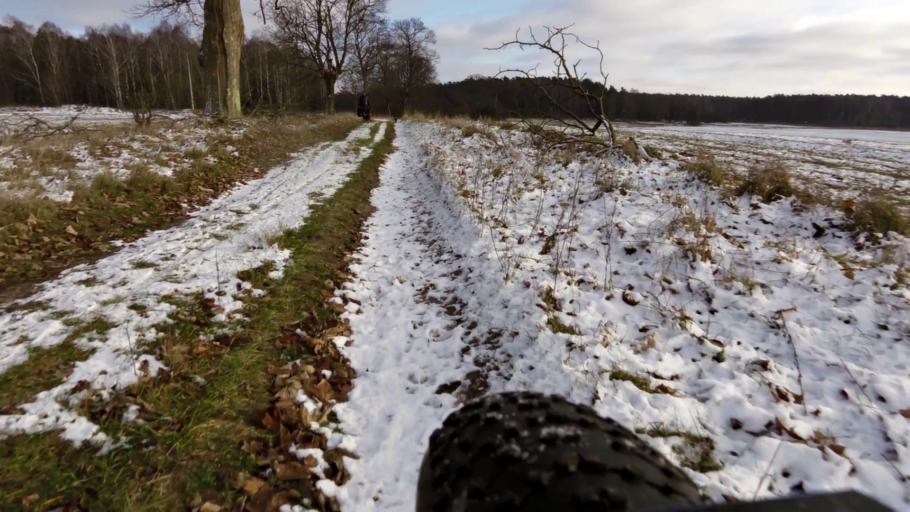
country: PL
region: West Pomeranian Voivodeship
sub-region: Powiat walecki
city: Tuczno
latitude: 53.3007
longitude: 16.2807
